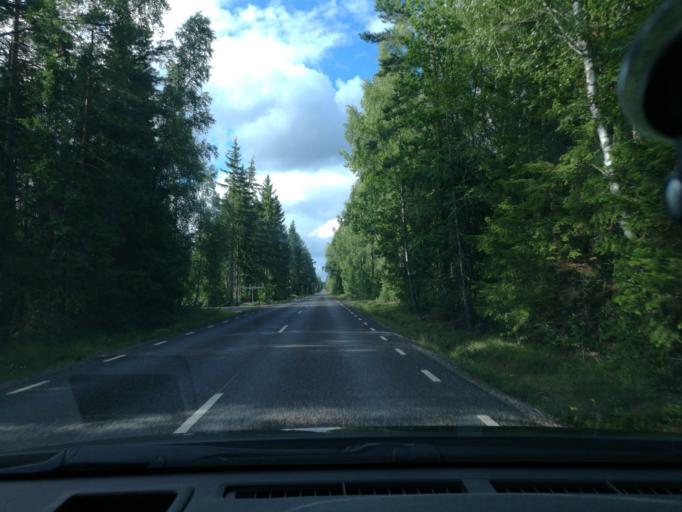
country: SE
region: Kronoberg
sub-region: Vaxjo Kommun
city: Braas
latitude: 57.0722
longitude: 15.0070
